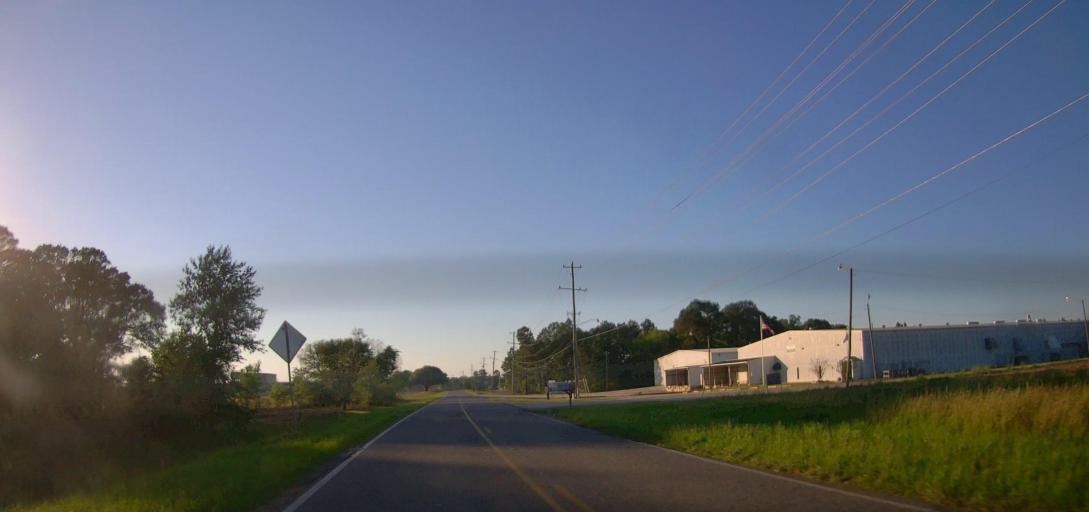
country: US
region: Georgia
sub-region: Ben Hill County
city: Fitzgerald
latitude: 31.6929
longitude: -83.2348
